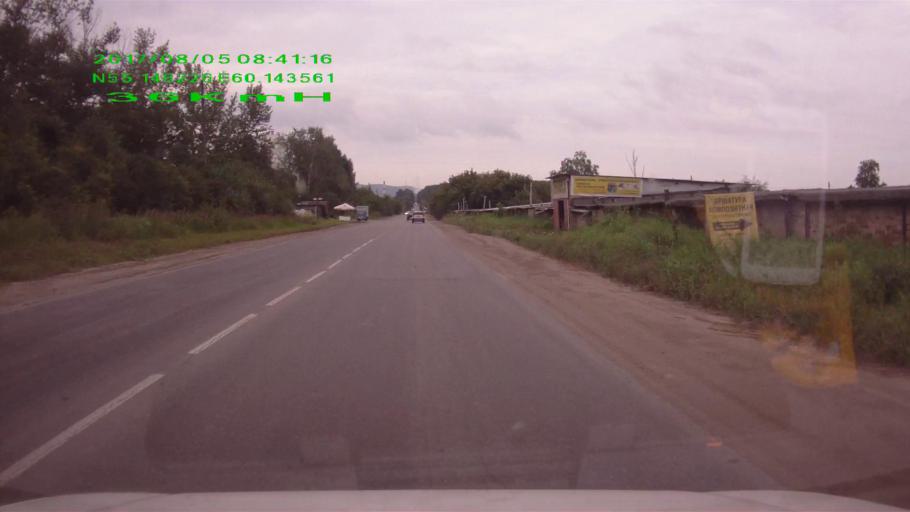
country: RU
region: Chelyabinsk
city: Turgoyak
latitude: 55.1460
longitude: 60.1435
